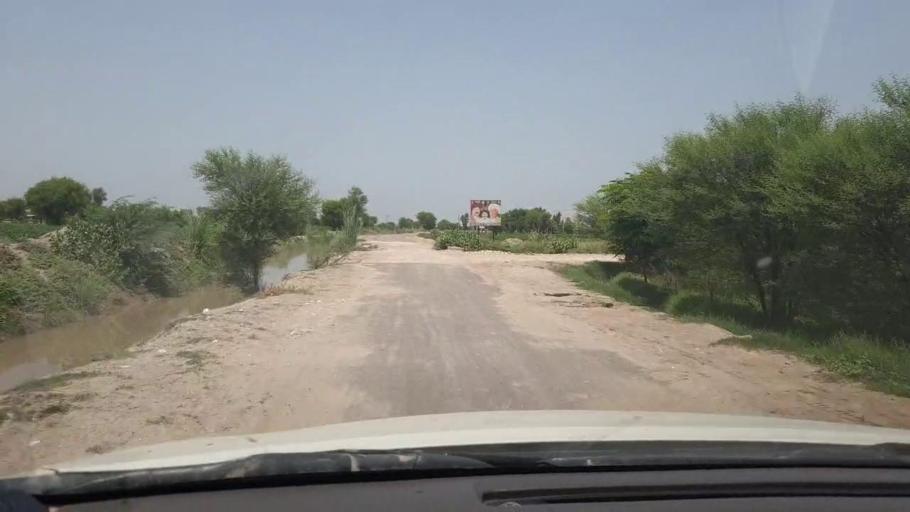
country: PK
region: Sindh
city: Rohri
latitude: 27.5233
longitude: 69.1781
